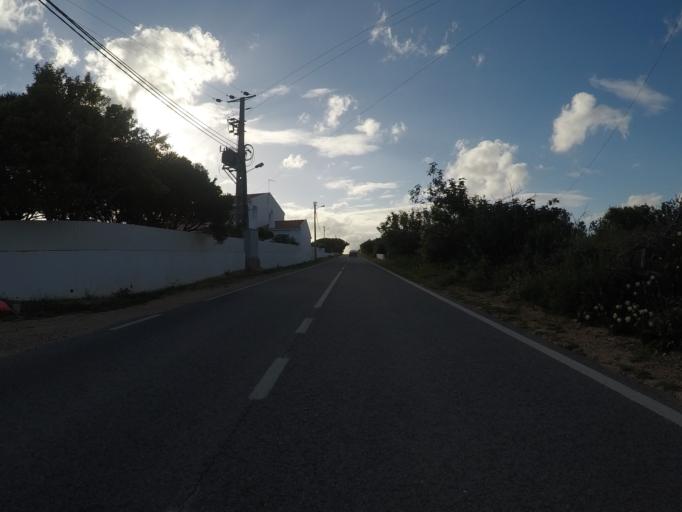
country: PT
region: Faro
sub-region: Lagoa
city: Carvoeiro
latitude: 37.0961
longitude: -8.4380
